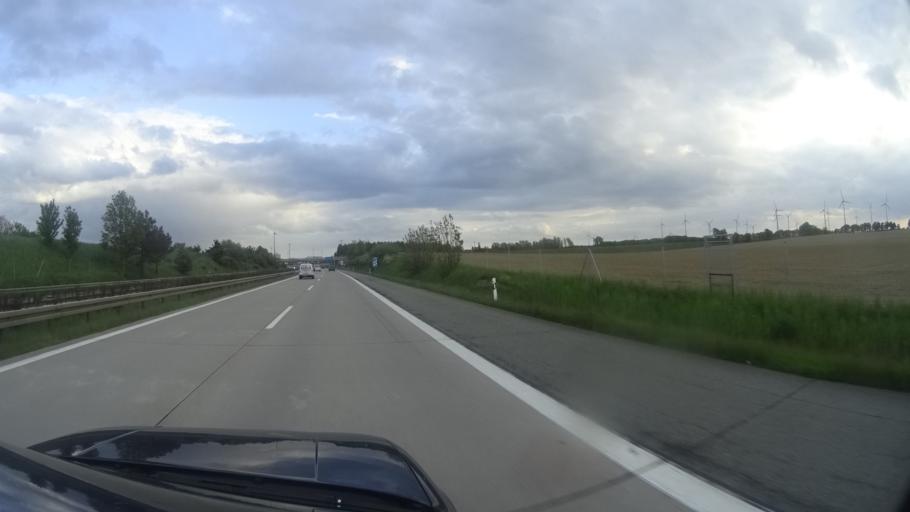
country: DE
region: Brandenburg
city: Wittstock
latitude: 53.1602
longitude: 12.4476
